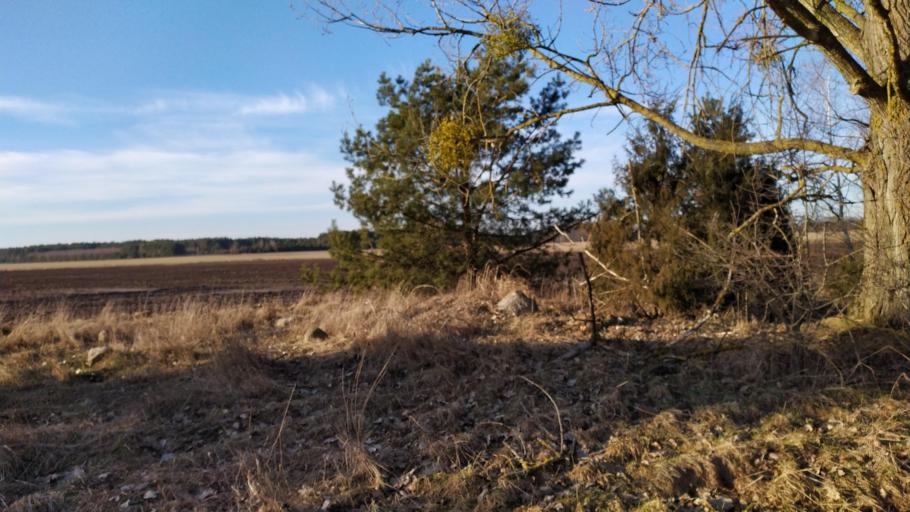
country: BY
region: Brest
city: Pruzhany
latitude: 52.5411
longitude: 24.2916
